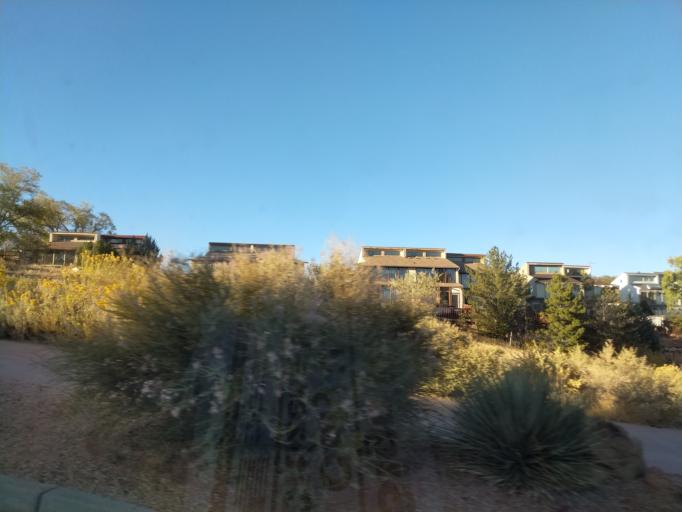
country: US
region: Colorado
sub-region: Mesa County
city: Redlands
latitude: 39.0567
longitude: -108.6192
